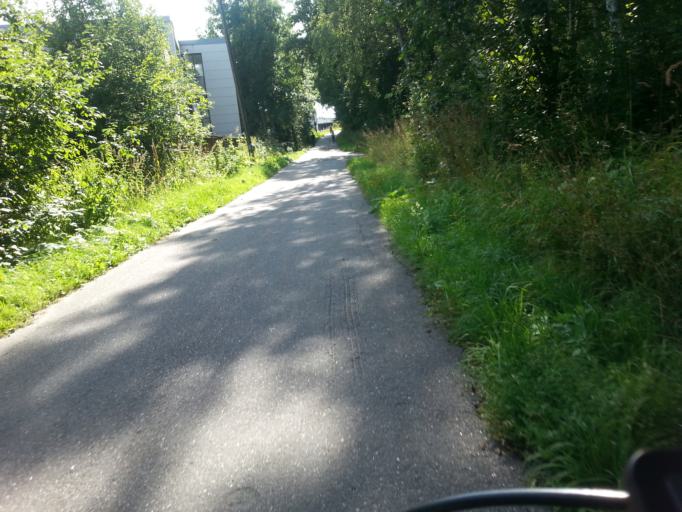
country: FI
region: Uusimaa
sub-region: Helsinki
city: Helsinki
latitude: 60.2214
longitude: 24.9917
